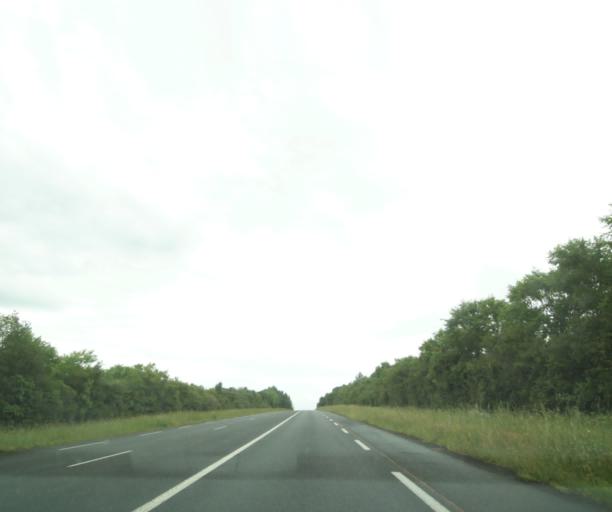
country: FR
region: Poitou-Charentes
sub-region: Departement des Deux-Sevres
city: Airvault
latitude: 46.7917
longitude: -0.2142
